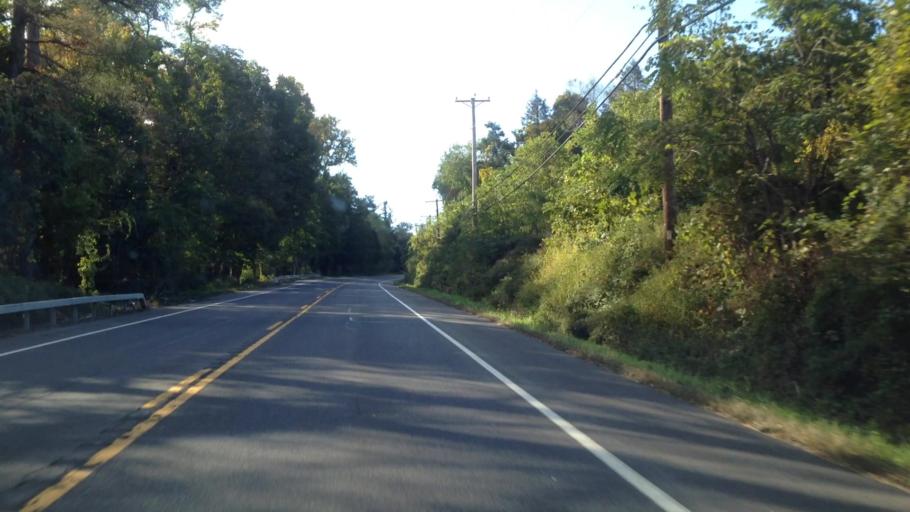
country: US
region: New York
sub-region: Dutchess County
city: Hyde Park
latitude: 41.7861
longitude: -73.9595
